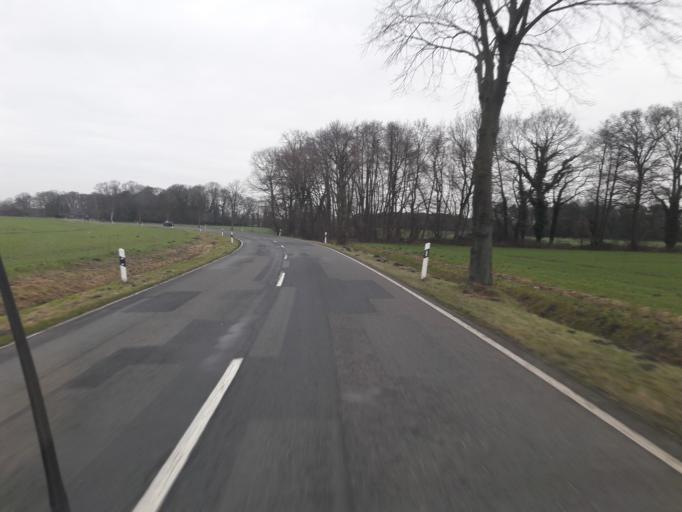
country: DE
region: Lower Saxony
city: Warmsen
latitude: 52.4045
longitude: 8.8603
